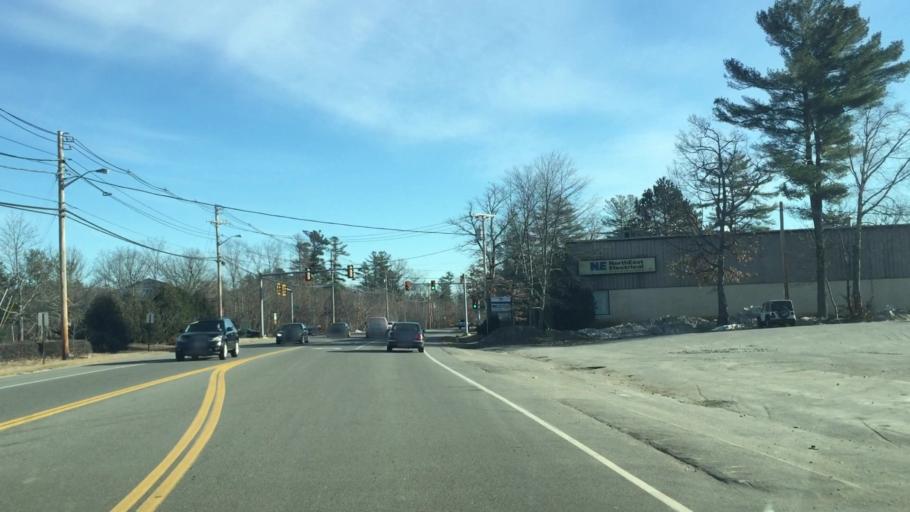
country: US
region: New Hampshire
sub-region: Rockingham County
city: Salem
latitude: 42.7646
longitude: -71.2479
